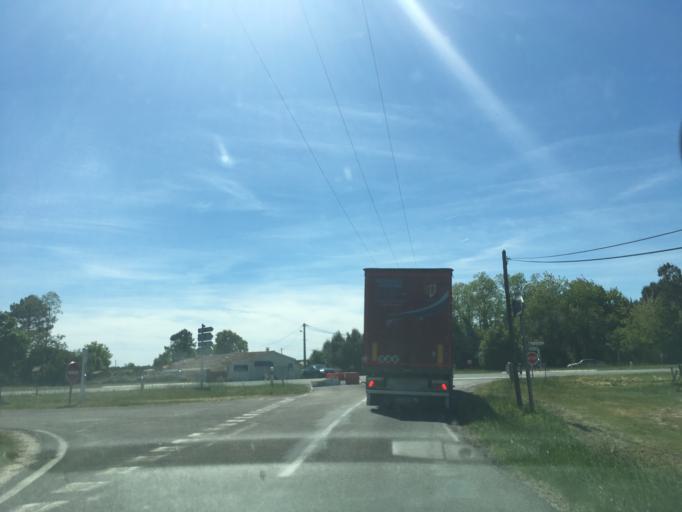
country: FR
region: Aquitaine
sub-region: Departement de la Gironde
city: Lesparre-Medoc
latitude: 45.2638
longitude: -0.9056
